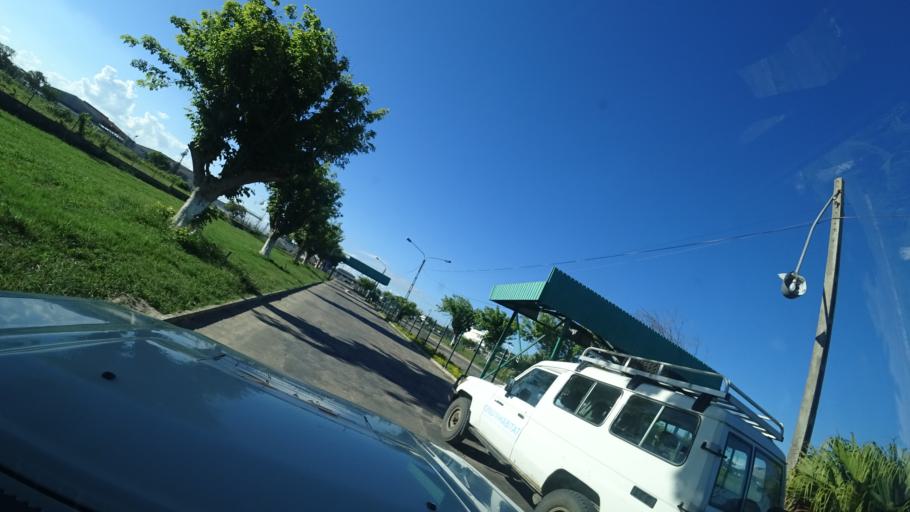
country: MZ
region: Sofala
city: Beira
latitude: -19.8000
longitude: 34.9001
